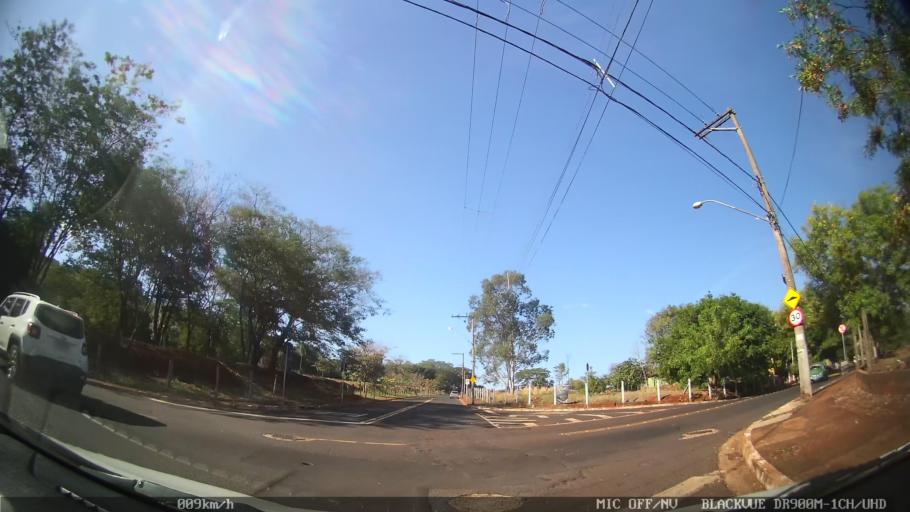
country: BR
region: Sao Paulo
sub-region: Ribeirao Preto
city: Ribeirao Preto
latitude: -21.1696
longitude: -47.7865
